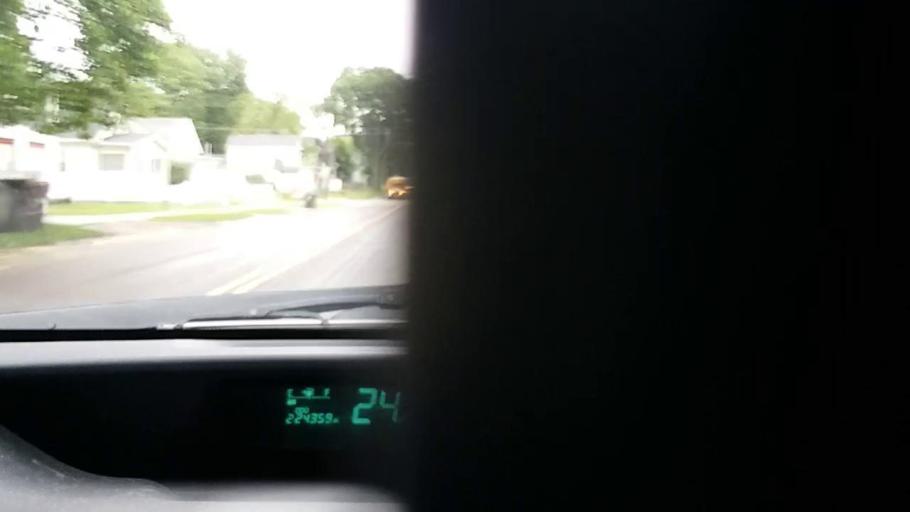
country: US
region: Illinois
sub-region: Peoria County
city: Peoria
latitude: 40.7024
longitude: -89.6036
